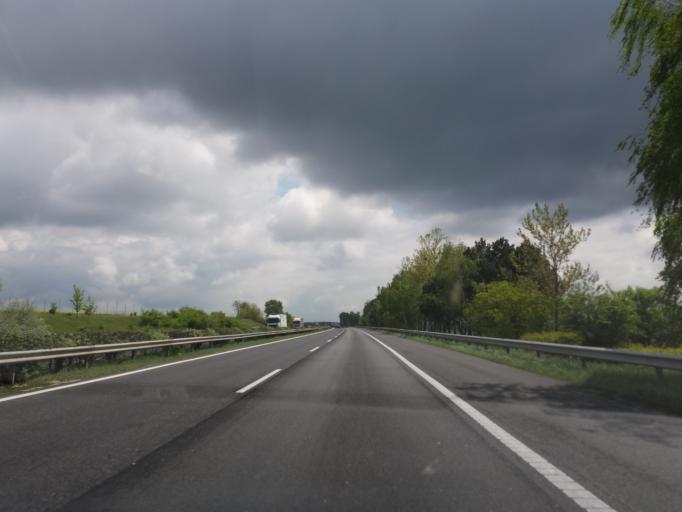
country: HU
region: Komarom-Esztergom
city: Kocs
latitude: 47.6439
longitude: 18.2137
